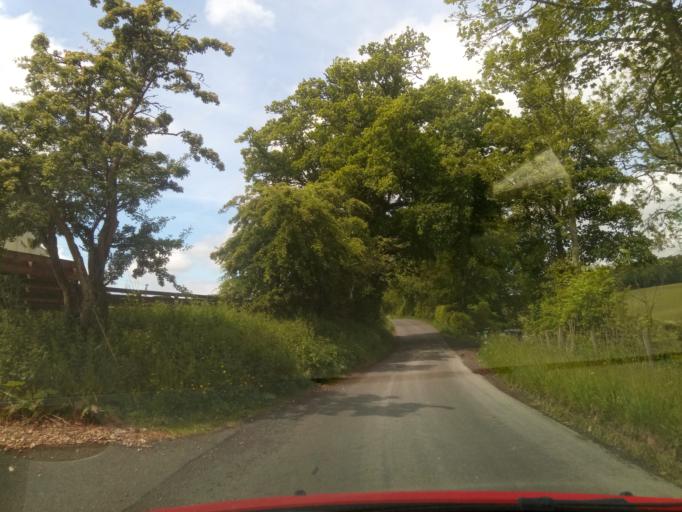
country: GB
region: Scotland
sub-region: The Scottish Borders
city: Selkirk
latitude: 55.5143
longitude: -2.7889
